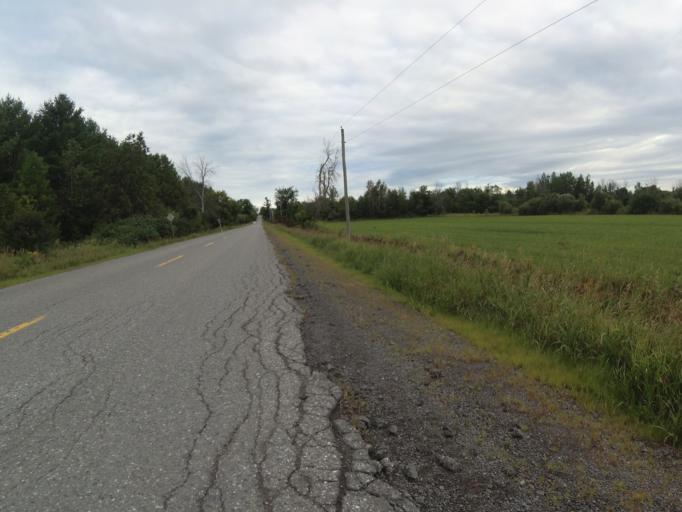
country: CA
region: Ontario
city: Clarence-Rockland
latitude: 45.4204
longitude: -75.2946
